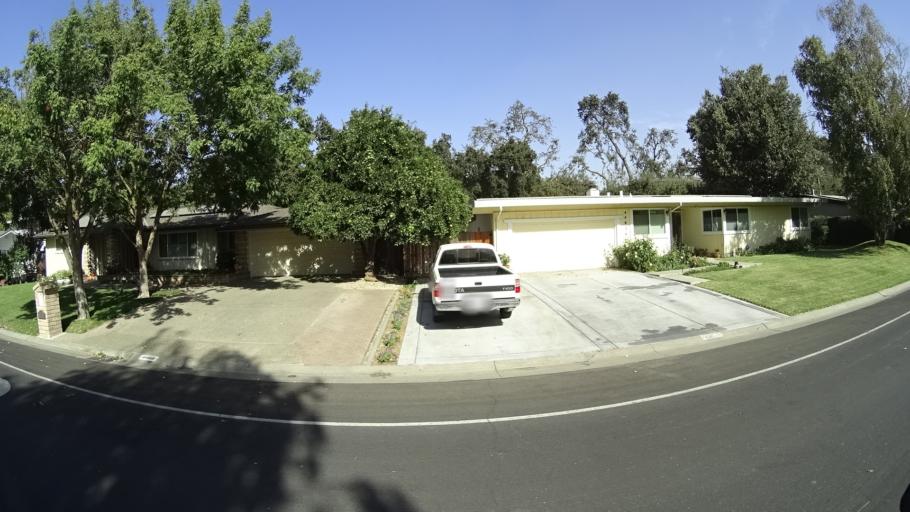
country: US
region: California
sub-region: Yolo County
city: Davis
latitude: 38.5478
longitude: -121.6829
